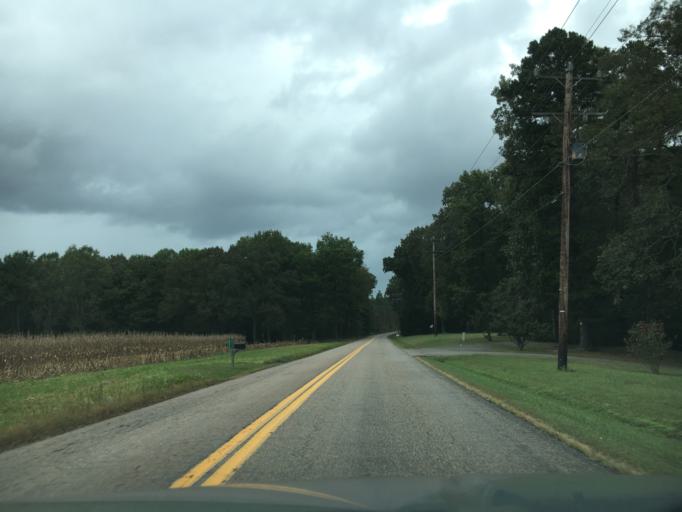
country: US
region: Virginia
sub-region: Amelia County
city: Amelia Court House
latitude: 37.3628
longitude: -77.9755
